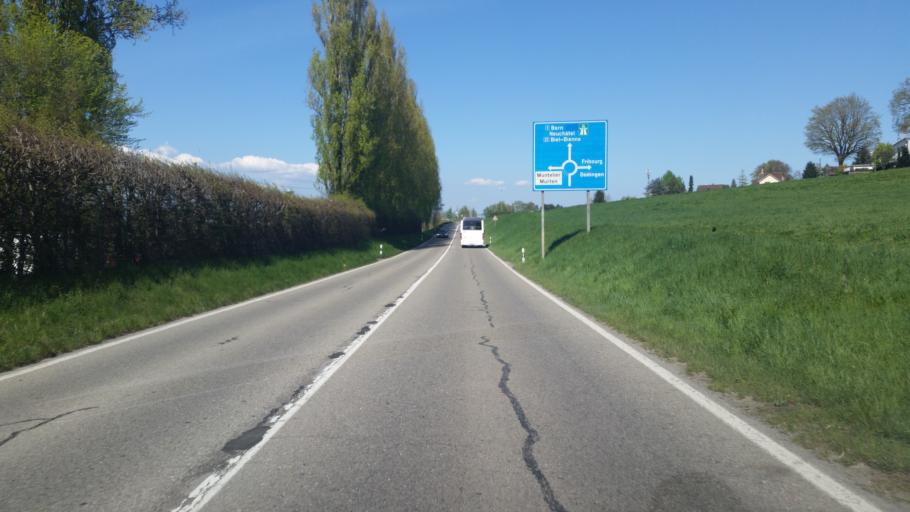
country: CH
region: Fribourg
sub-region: See District
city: Murten
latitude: 46.9417
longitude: 7.1479
